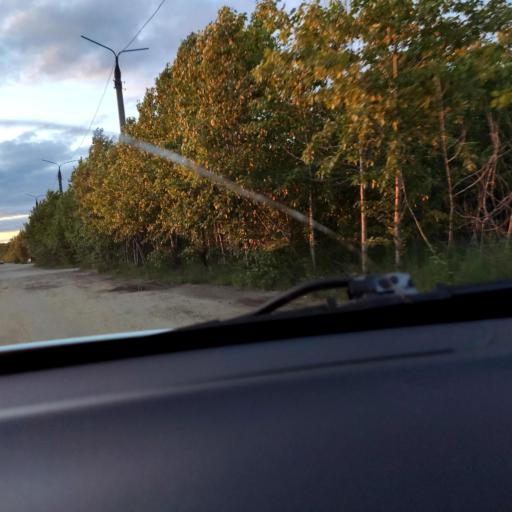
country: RU
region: Tatarstan
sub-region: Gorod Kazan'
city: Kazan
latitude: 55.7862
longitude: 49.0972
